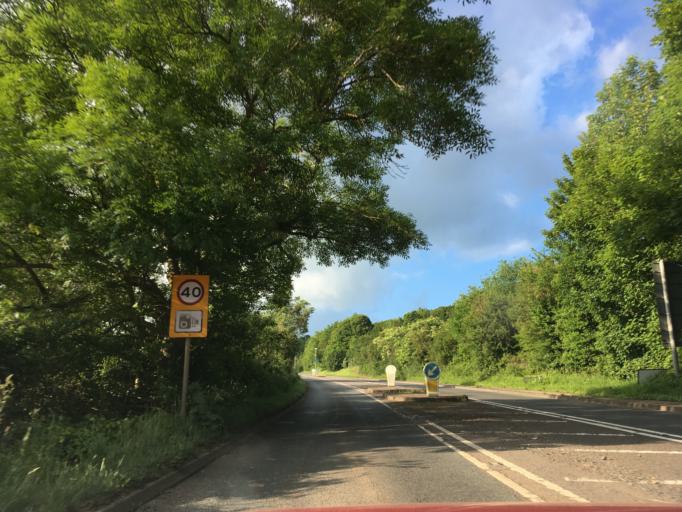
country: GB
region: England
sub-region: Somerset
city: Axbridge
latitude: 51.2914
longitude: -2.8325
